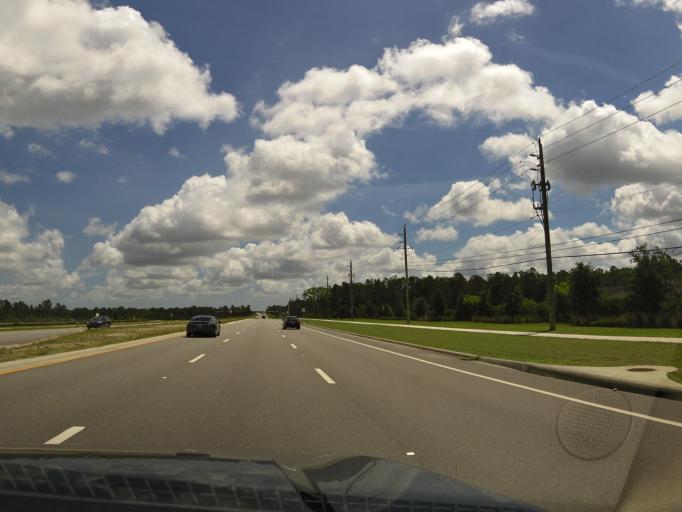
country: US
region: Florida
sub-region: Saint Johns County
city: Palm Valley
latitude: 30.0843
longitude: -81.4742
